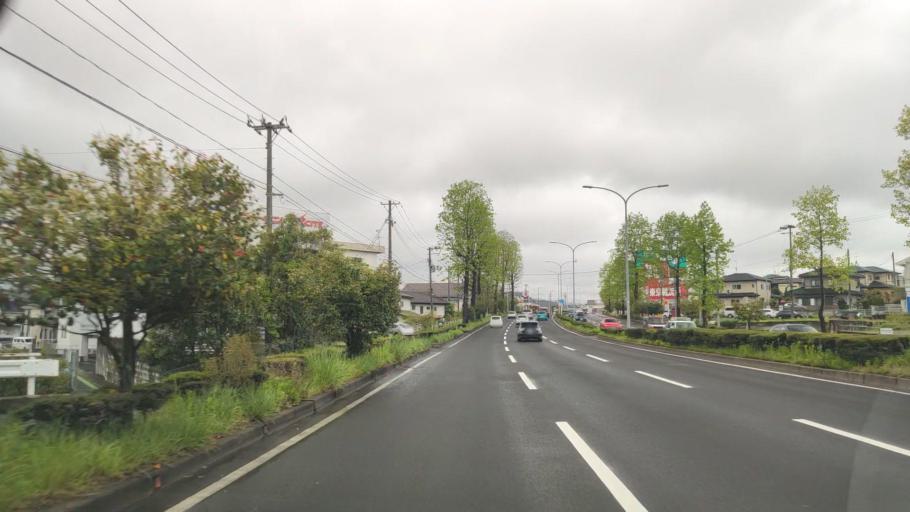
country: JP
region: Miyagi
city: Sendai
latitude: 38.2222
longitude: 140.8620
